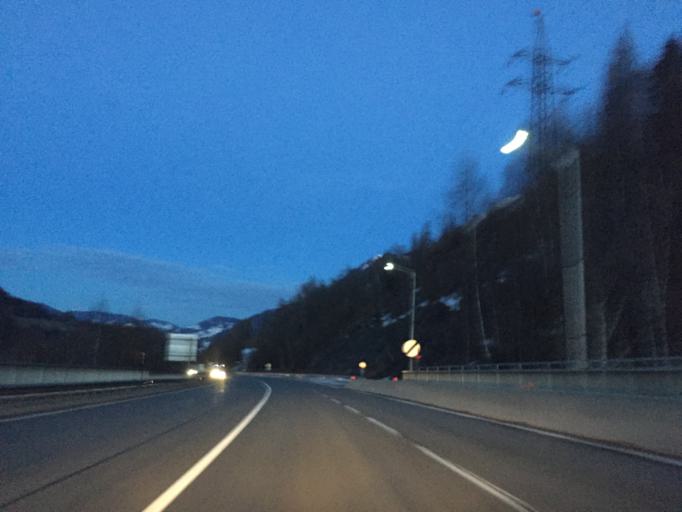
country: AT
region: Salzburg
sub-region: Politischer Bezirk Zell am See
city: Lend
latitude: 47.2944
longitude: 13.0588
